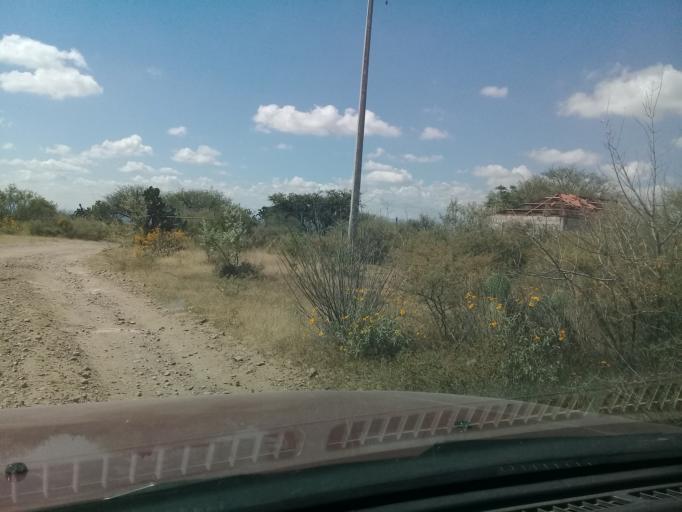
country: MX
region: Aguascalientes
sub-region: Aguascalientes
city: San Sebastian [Fraccionamiento]
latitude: 21.7796
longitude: -102.2505
